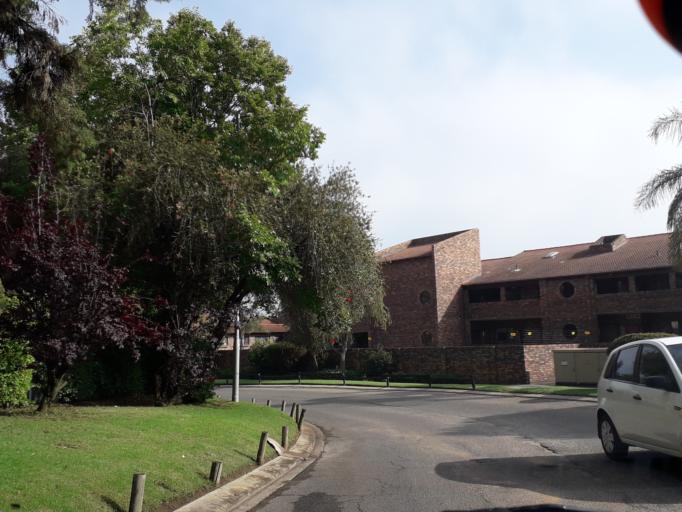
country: ZA
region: Gauteng
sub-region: City of Johannesburg Metropolitan Municipality
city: Johannesburg
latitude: -26.0824
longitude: 28.0329
